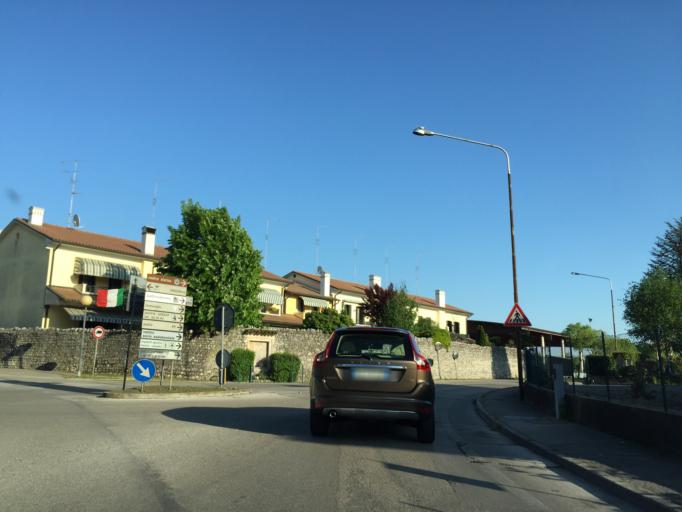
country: IT
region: Friuli Venezia Giulia
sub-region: Provincia di Pordenone
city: Porcia
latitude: 45.9591
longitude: 12.6080
